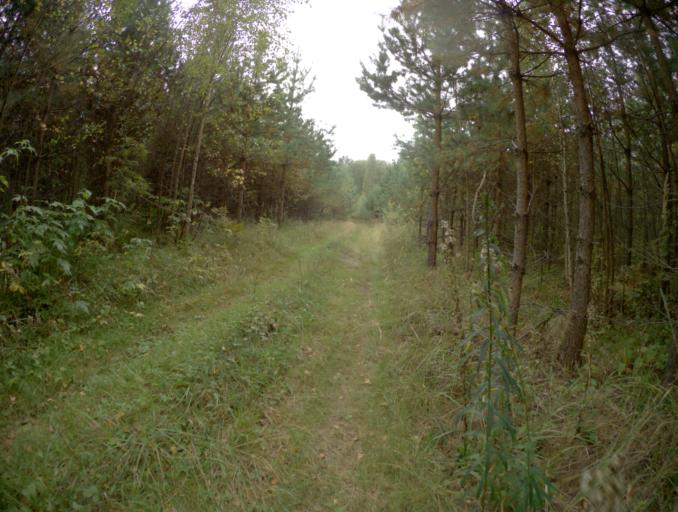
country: RU
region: Vladimir
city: Ivanishchi
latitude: 55.8274
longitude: 40.2990
